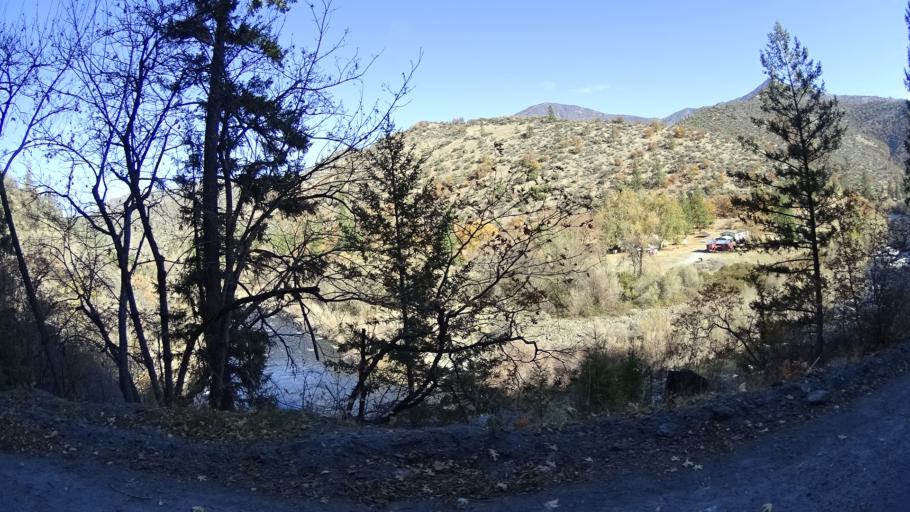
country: US
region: California
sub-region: Siskiyou County
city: Yreka
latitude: 41.8477
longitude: -122.6937
